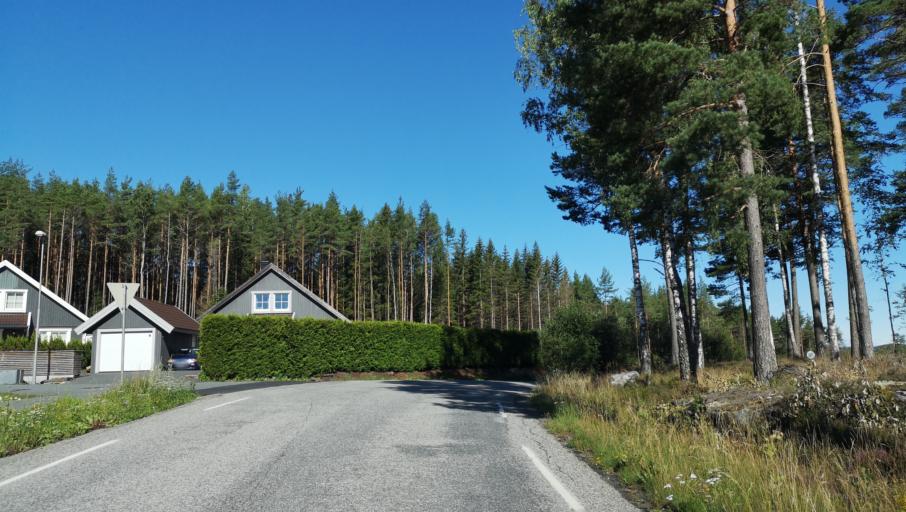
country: NO
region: Ostfold
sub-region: Hobol
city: Knappstad
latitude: 59.6315
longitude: 11.0247
